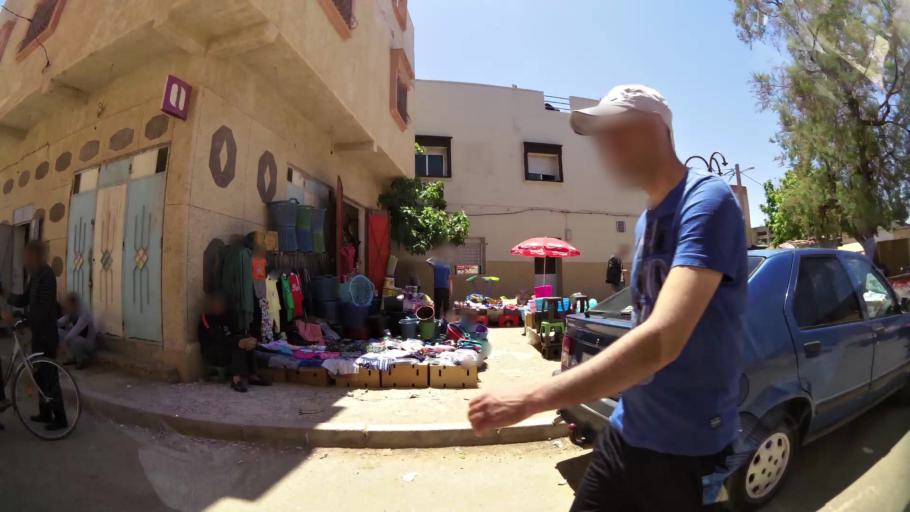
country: MA
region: Oriental
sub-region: Oujda-Angad
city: Oujda
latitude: 34.6718
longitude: -1.9285
